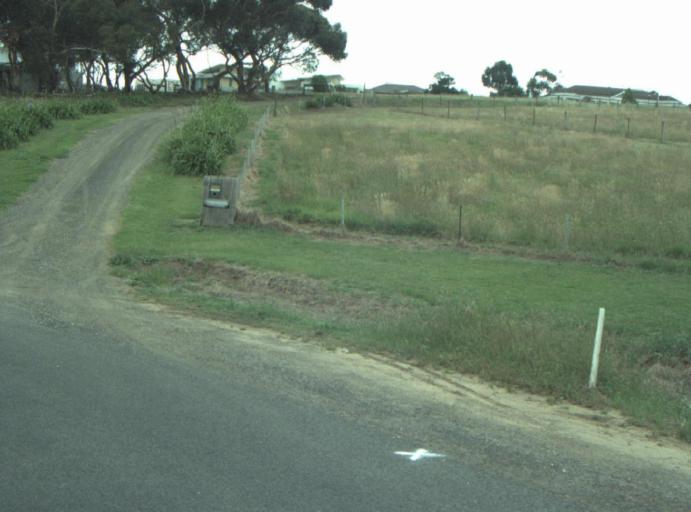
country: AU
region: Victoria
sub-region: Greater Geelong
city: Wandana Heights
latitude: -38.1799
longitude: 144.3046
